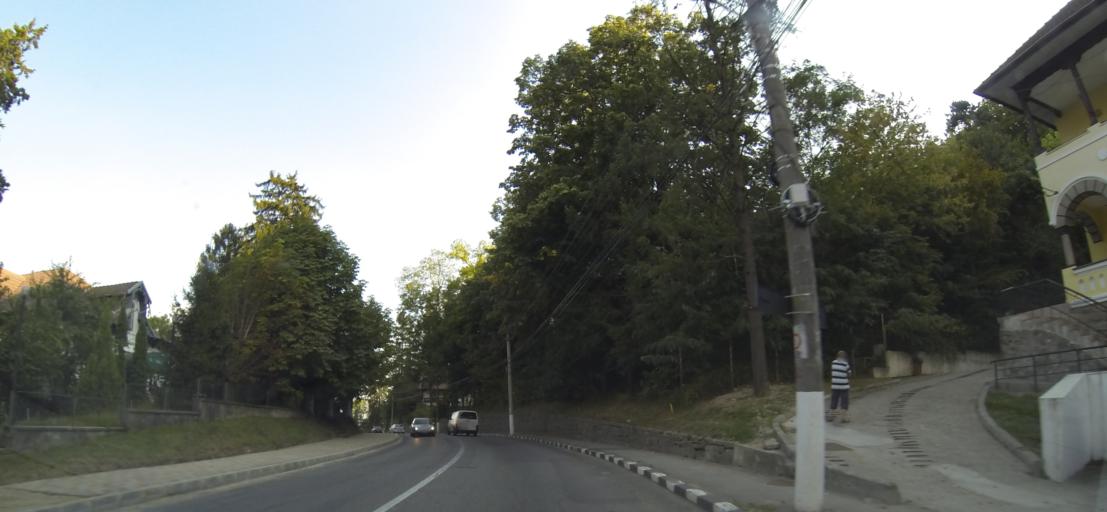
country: RO
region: Valcea
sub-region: Oras Calimanesti
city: Jiblea Veche
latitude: 45.2527
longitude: 24.3354
